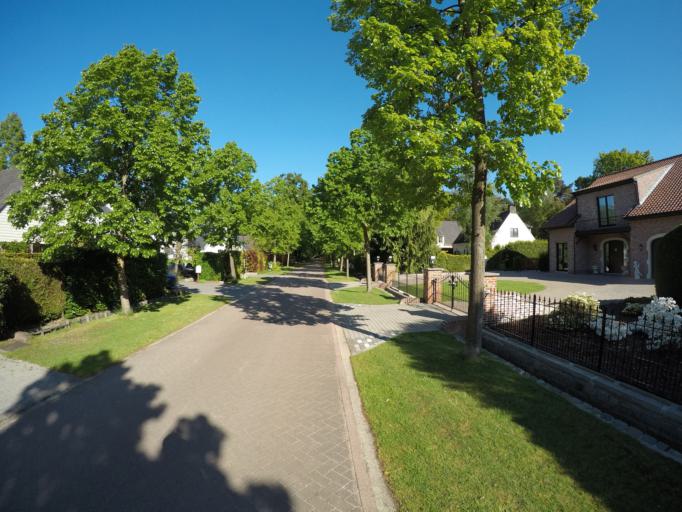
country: BE
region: Flanders
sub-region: Provincie Antwerpen
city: Schilde
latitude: 51.2610
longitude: 4.5813
